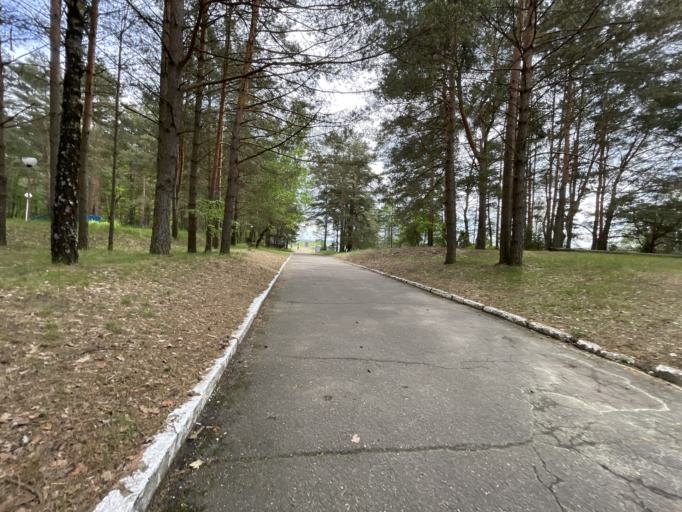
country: BY
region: Minsk
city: Stowbtsy
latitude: 53.4255
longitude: 26.8150
